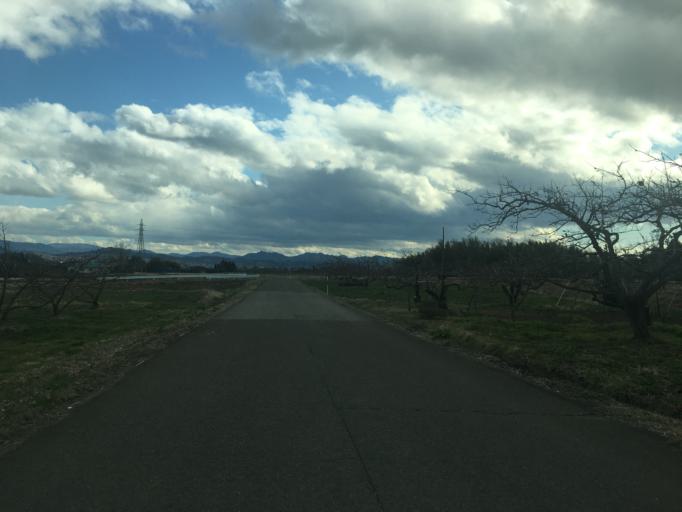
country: JP
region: Fukushima
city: Yanagawamachi-saiwaicho
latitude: 37.8824
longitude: 140.5866
